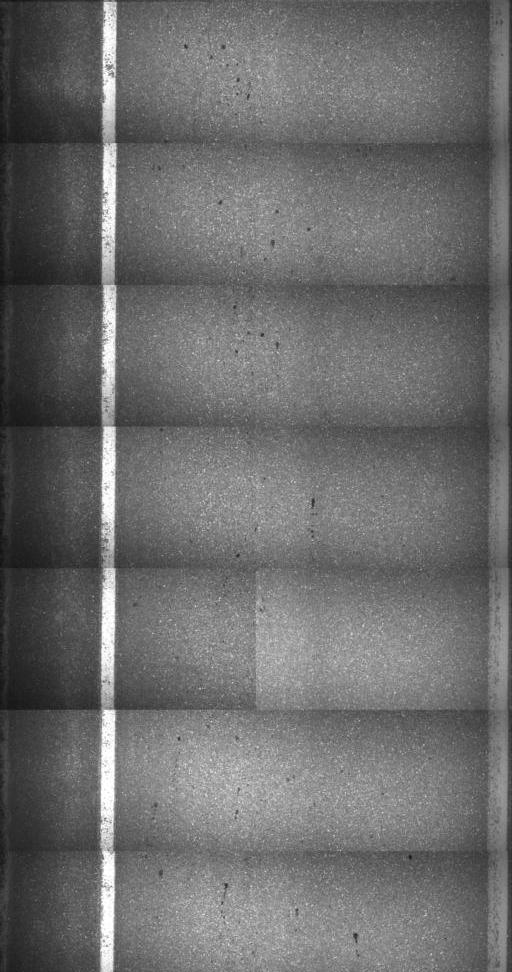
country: US
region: New Hampshire
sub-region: Coos County
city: Lancaster
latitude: 44.5114
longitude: -71.5939
